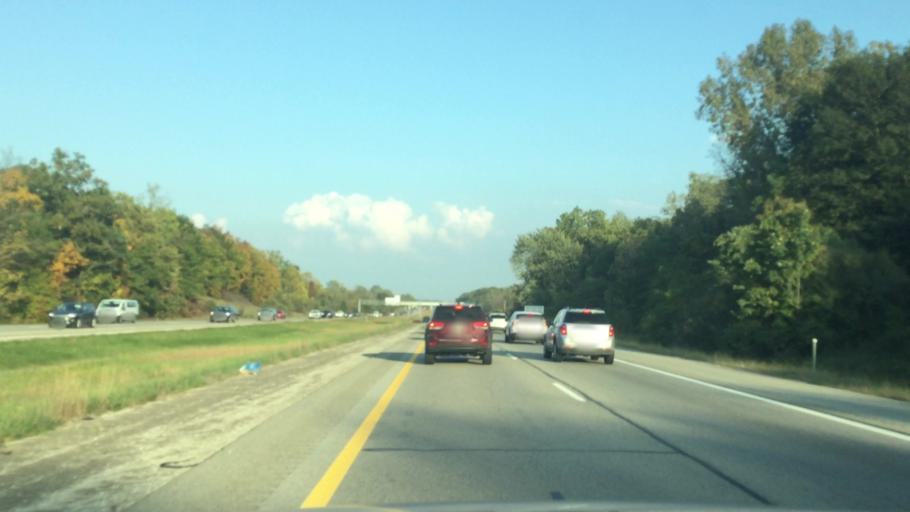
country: US
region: Michigan
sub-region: Washtenaw County
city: Ann Arbor
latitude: 42.3252
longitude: -83.6735
